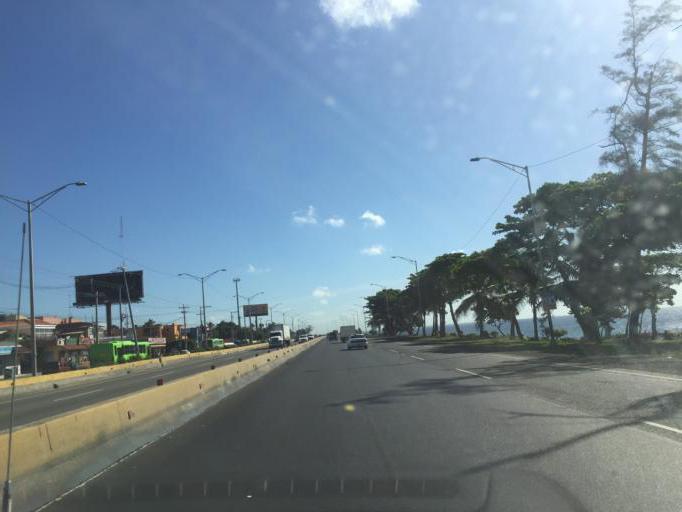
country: DO
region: Santo Domingo
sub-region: Santo Domingo
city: Santo Domingo Este
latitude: 18.4648
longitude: -69.8142
